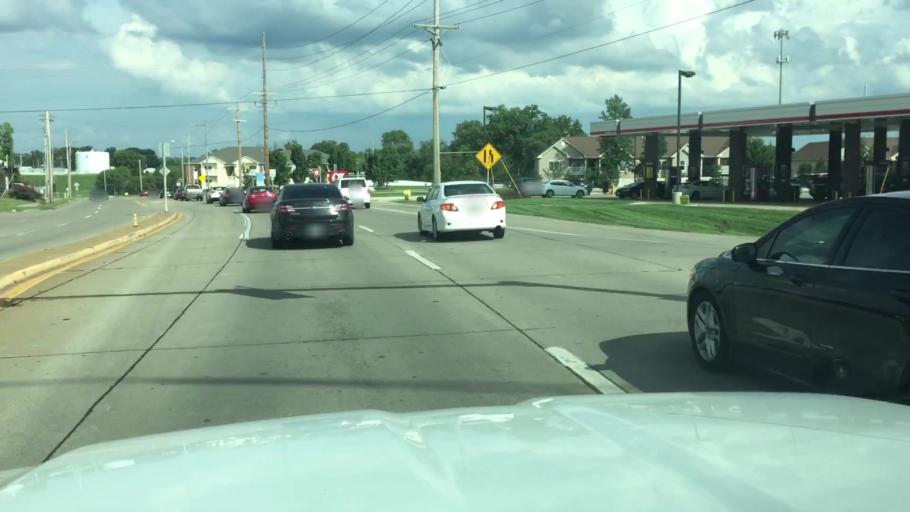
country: US
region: Missouri
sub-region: Jefferson County
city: Arnold
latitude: 38.4616
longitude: -90.3731
